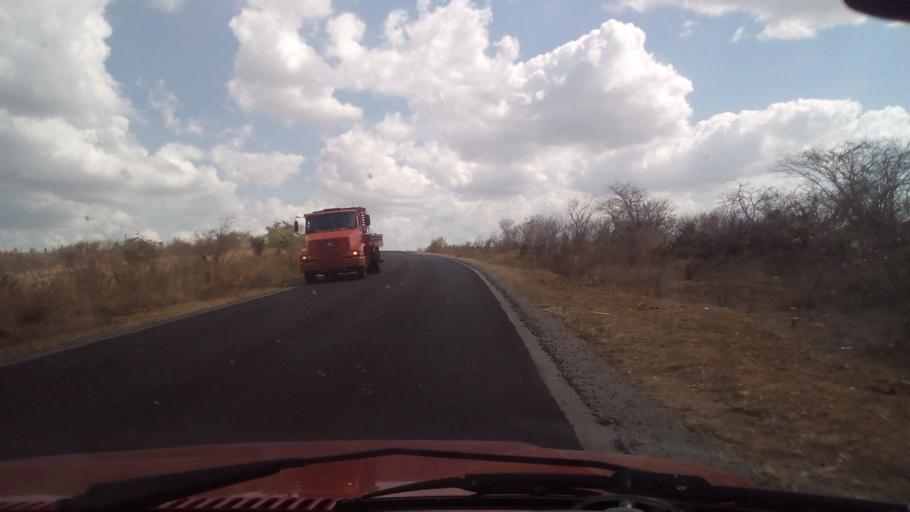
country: BR
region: Paraiba
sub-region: Bananeiras
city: Bananeiras
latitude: -6.7287
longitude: -35.7098
